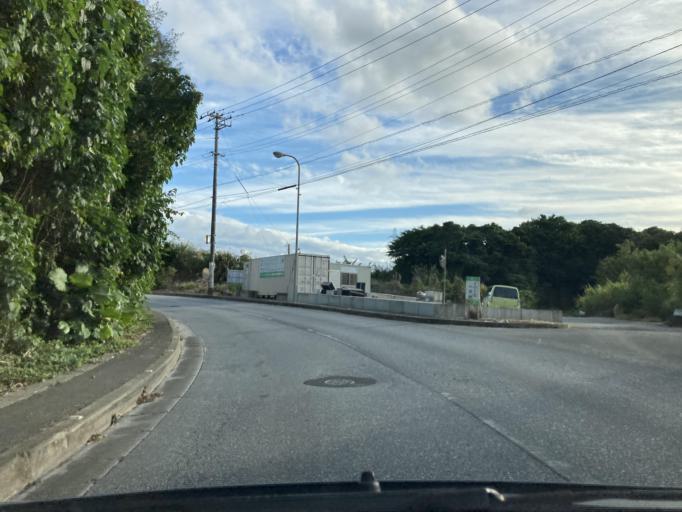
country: JP
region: Okinawa
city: Tomigusuku
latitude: 26.1471
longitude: 127.7442
